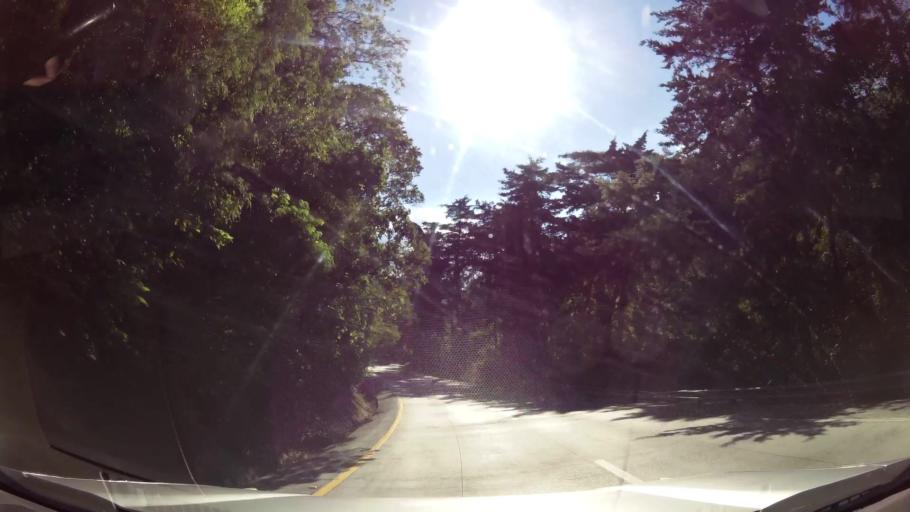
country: GT
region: Sacatepequez
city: Santa Lucia Milpas Altas
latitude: 14.5664
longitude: -90.7001
